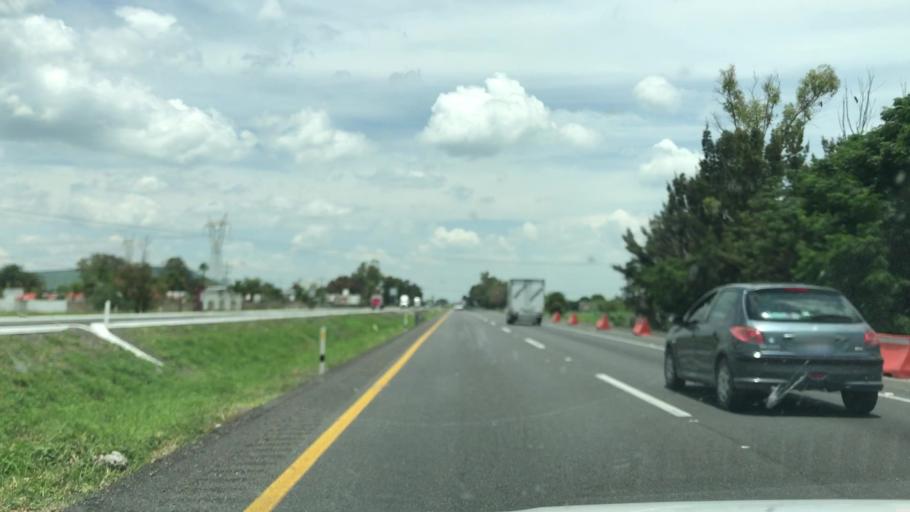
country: MX
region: Guanajuato
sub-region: Salamanca
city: El Divisador
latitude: 20.5974
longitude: -101.1760
